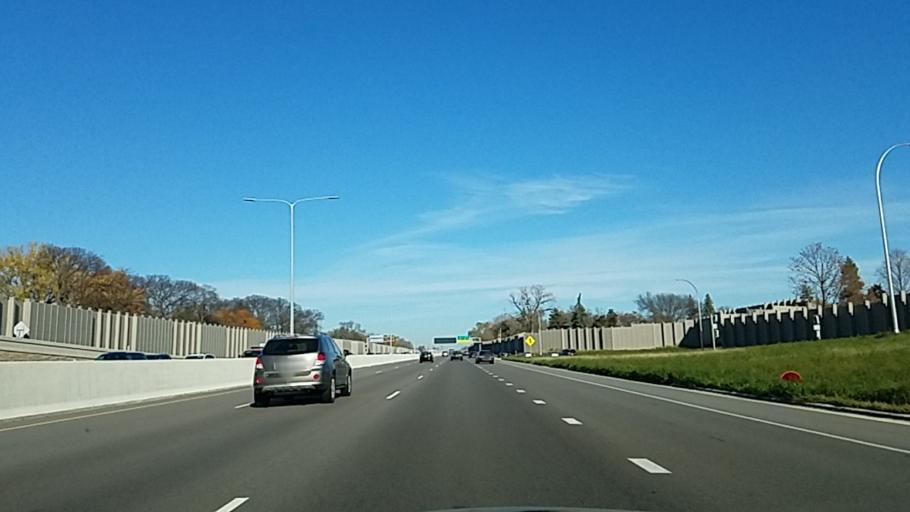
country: US
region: Minnesota
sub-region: Hennepin County
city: Saint Louis Park
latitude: 44.9489
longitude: -93.3479
